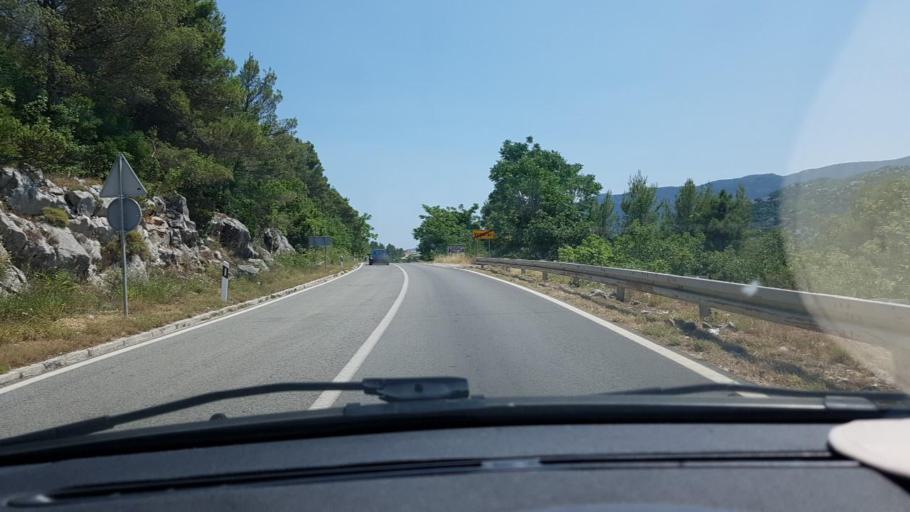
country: HR
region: Splitsko-Dalmatinska
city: Vrgorac
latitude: 43.1981
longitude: 17.3767
